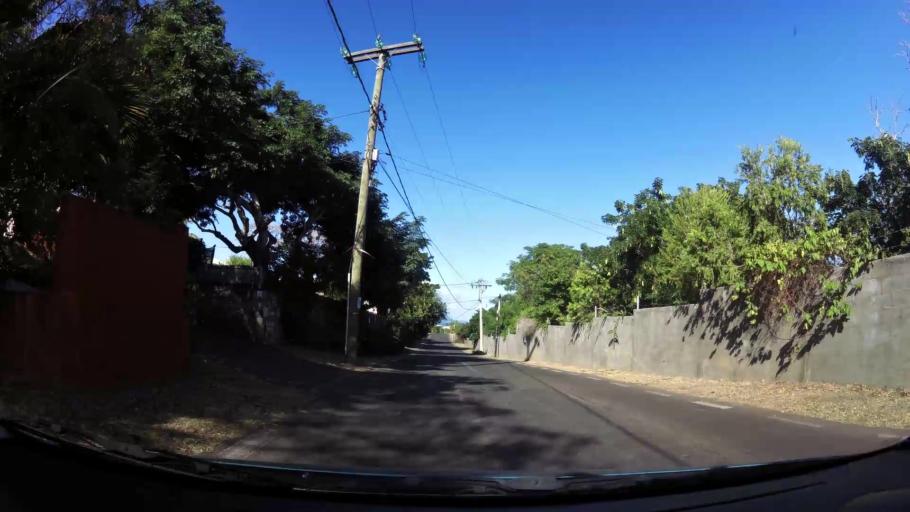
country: MU
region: Black River
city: Grande Riviere Noire
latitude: -20.3449
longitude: 57.3671
